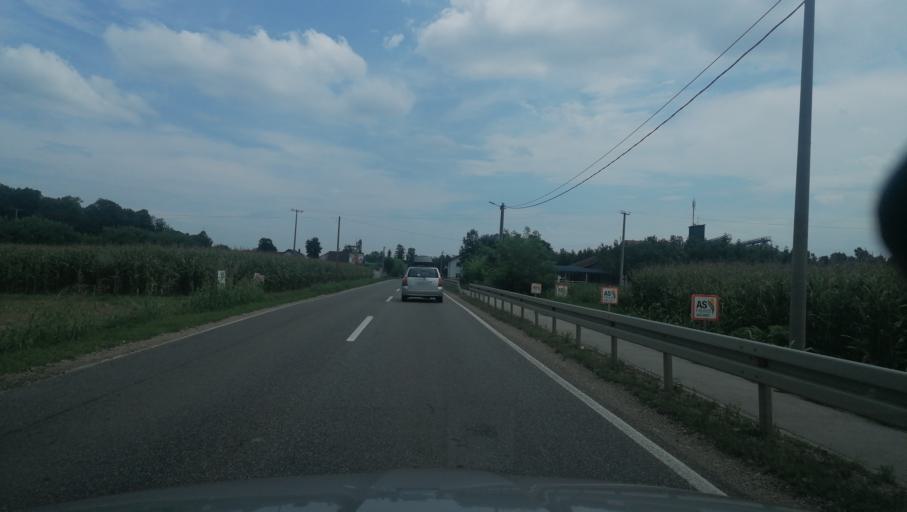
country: BA
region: Republika Srpska
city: Obudovac
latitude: 44.9548
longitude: 18.6395
